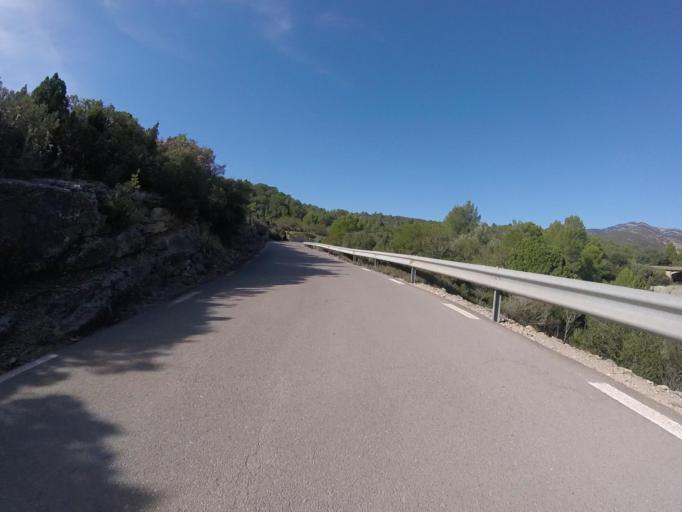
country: ES
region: Valencia
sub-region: Provincia de Castello
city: Sarratella
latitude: 40.2715
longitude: 0.0399
